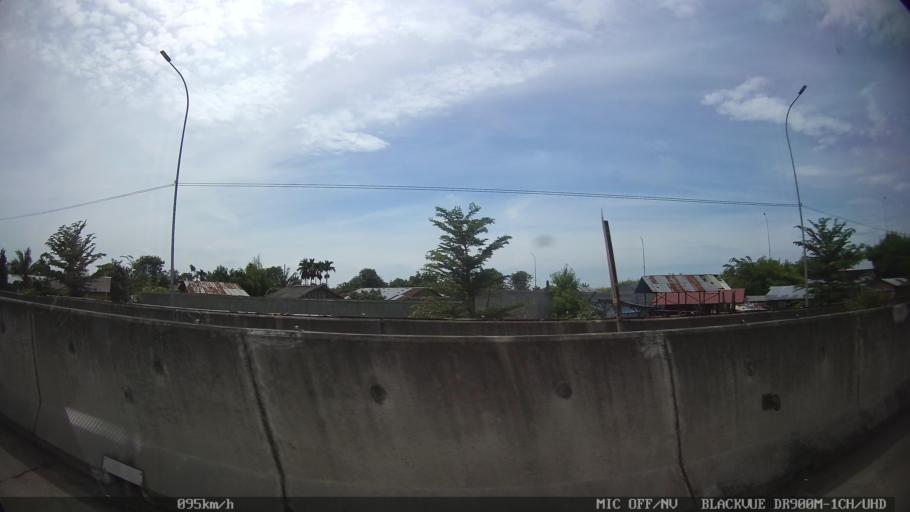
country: ID
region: North Sumatra
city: Medan
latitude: 3.6435
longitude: 98.6479
